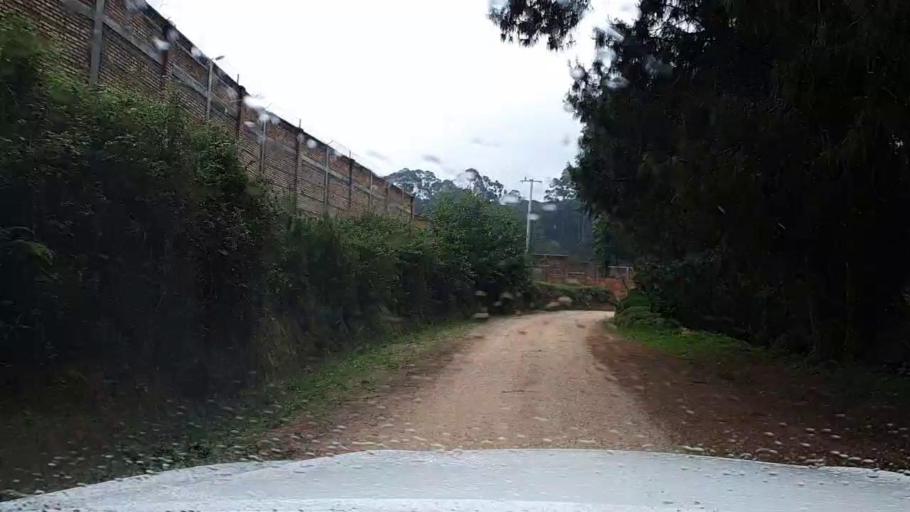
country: RW
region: Southern Province
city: Nzega
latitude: -2.3677
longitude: 29.3798
